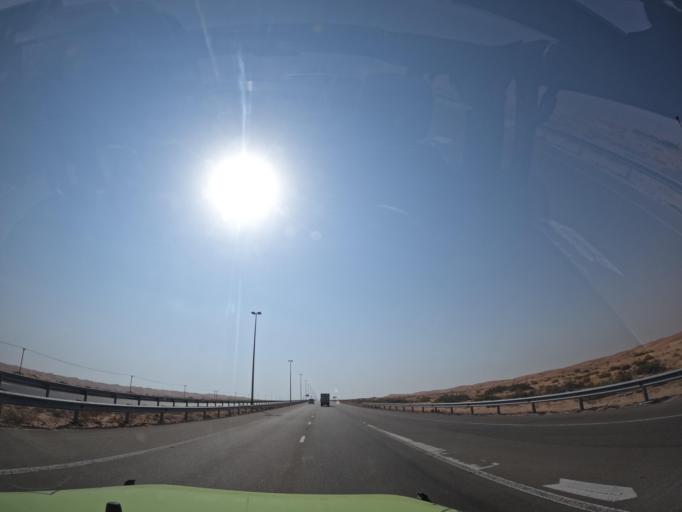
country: OM
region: Al Buraimi
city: Al Buraymi
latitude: 24.4363
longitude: 55.6704
